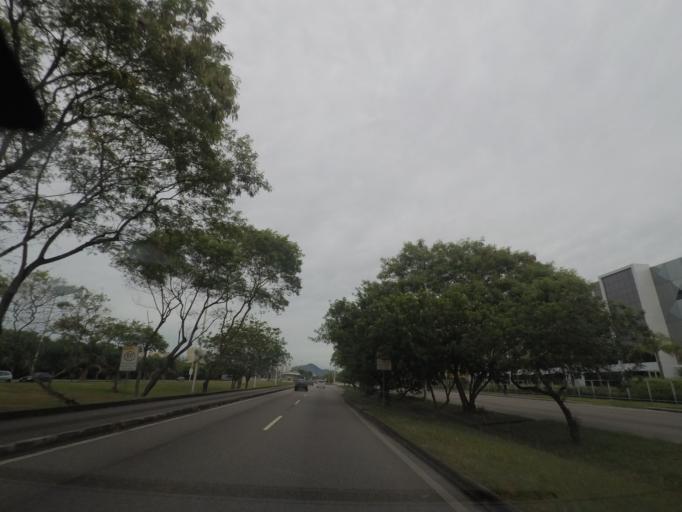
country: BR
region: Rio de Janeiro
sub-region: Nilopolis
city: Nilopolis
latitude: -23.0020
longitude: -43.4219
